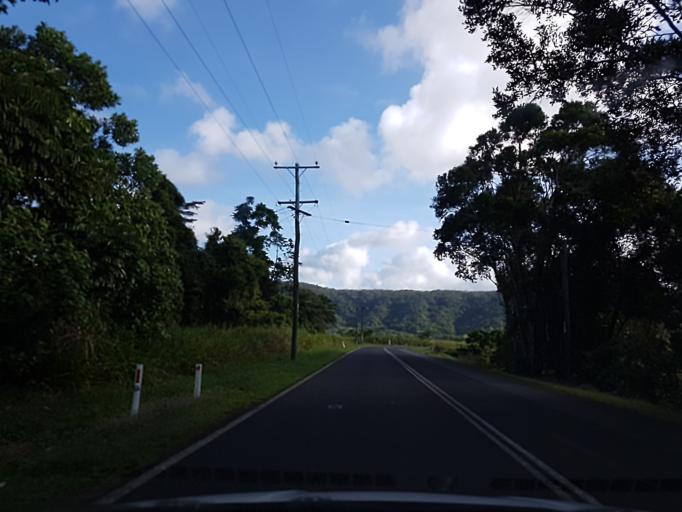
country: AU
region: Queensland
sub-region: Cairns
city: Port Douglas
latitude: -16.2765
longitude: 145.3882
